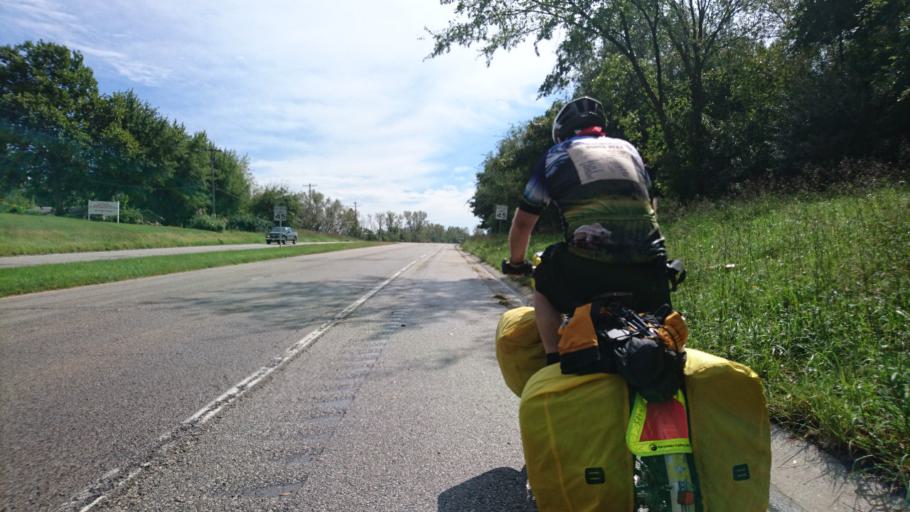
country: US
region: Illinois
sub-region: Sangamon County
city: Sherman
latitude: 39.8622
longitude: -89.6140
